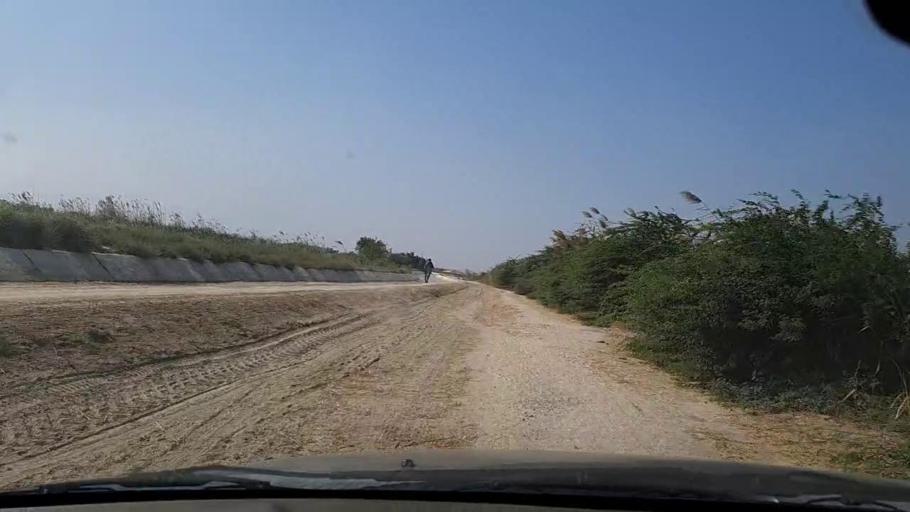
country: PK
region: Sindh
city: Chuhar Jamali
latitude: 24.4278
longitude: 67.8058
